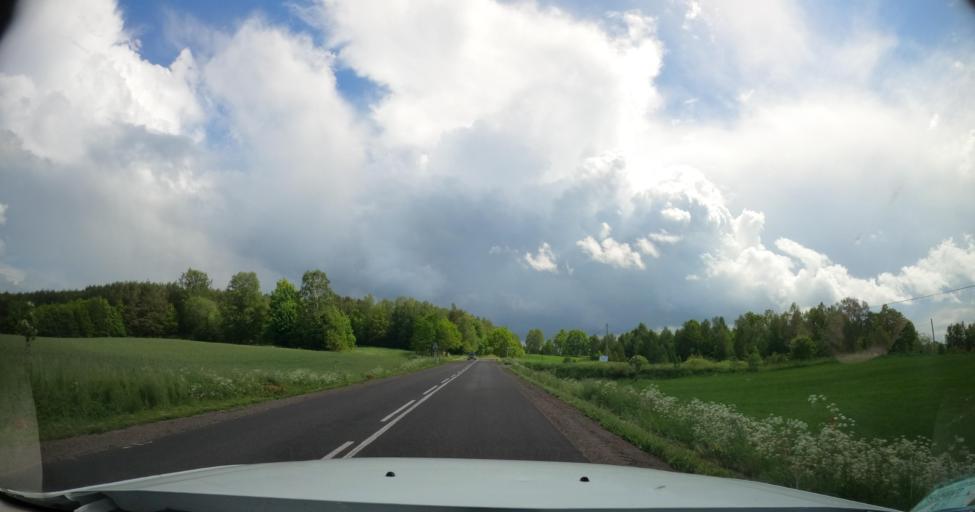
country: PL
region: Pomeranian Voivodeship
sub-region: Powiat bytowski
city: Czarna Dabrowka
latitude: 54.3497
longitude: 17.5805
